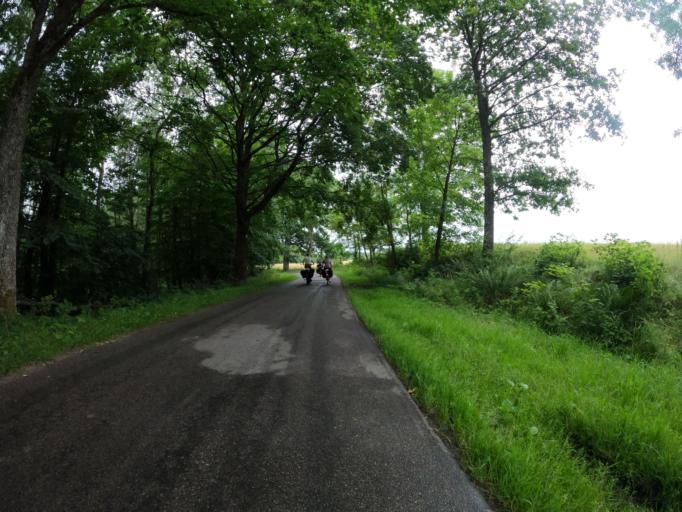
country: PL
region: West Pomeranian Voivodeship
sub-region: Powiat szczecinecki
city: Grzmiaca
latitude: 53.9063
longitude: 16.5019
